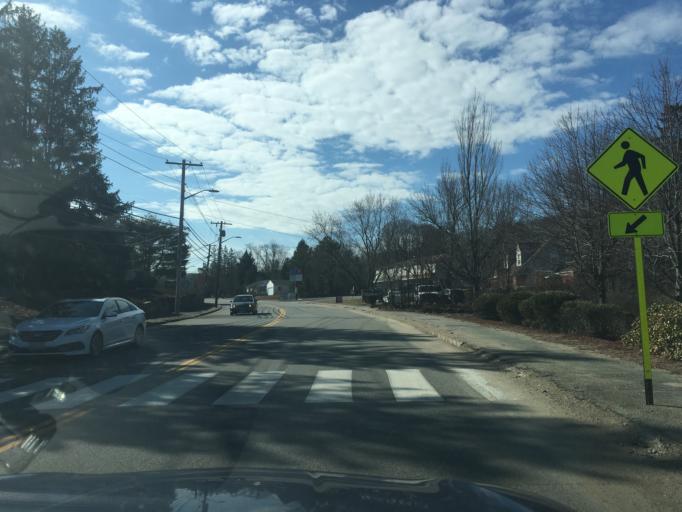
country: US
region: Rhode Island
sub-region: Providence County
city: Cranston
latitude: 41.7808
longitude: -71.4739
